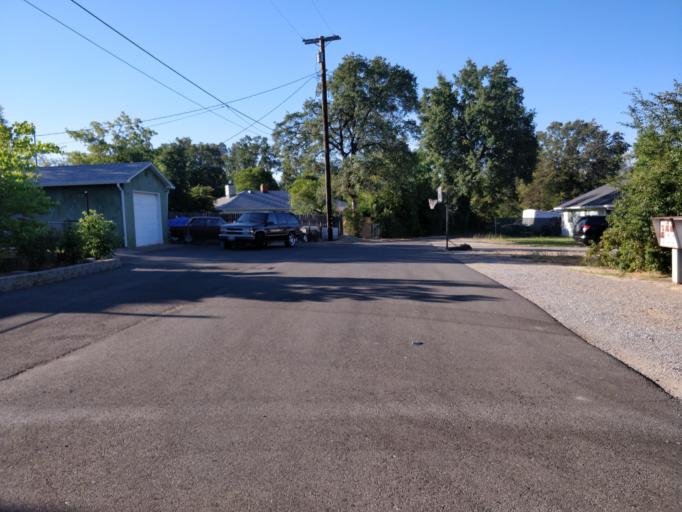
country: US
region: California
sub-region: Shasta County
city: Shasta Lake
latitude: 40.6774
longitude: -122.3555
